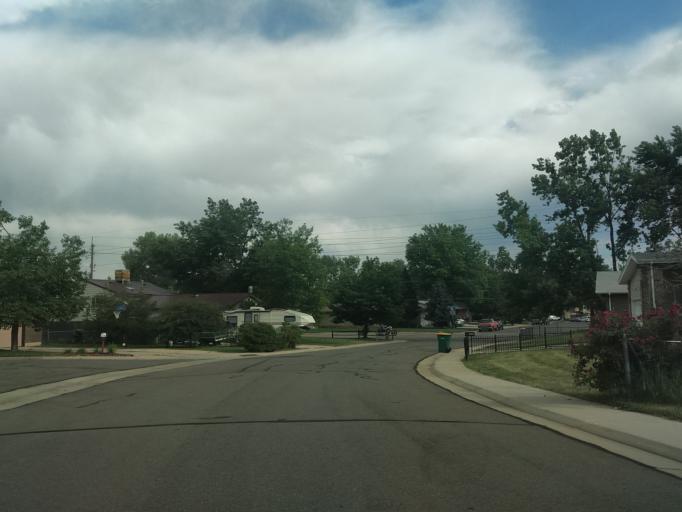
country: US
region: Colorado
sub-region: Jefferson County
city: Lakewood
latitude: 39.6974
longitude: -105.1098
